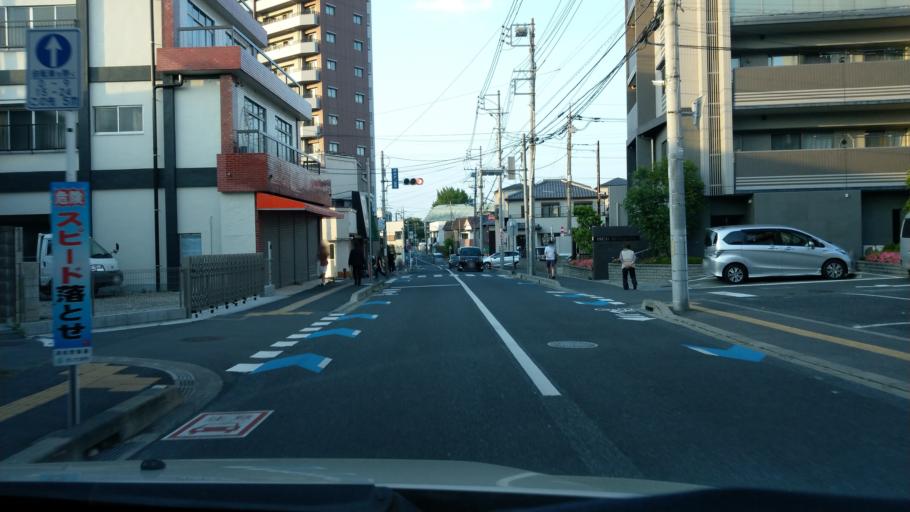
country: JP
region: Saitama
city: Yono
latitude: 35.8762
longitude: 139.6494
